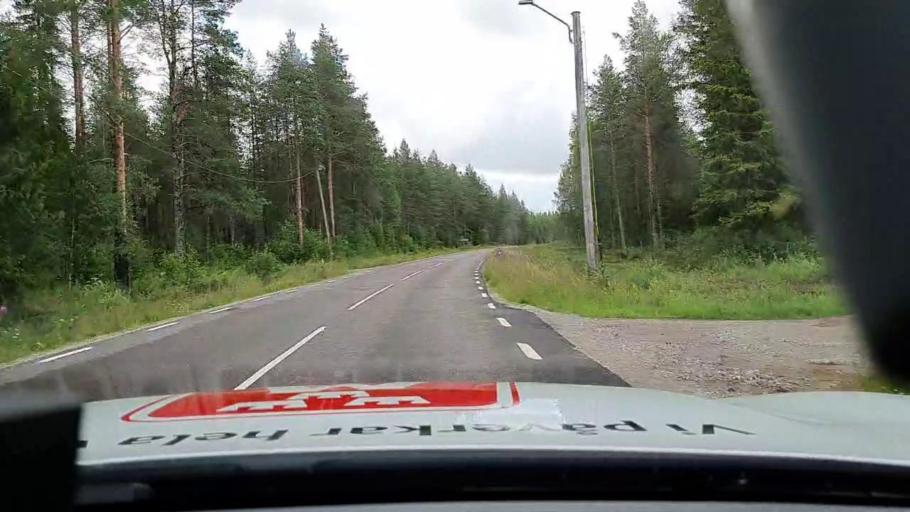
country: SE
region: Norrbotten
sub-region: Overkalix Kommun
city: OEverkalix
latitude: 66.2591
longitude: 22.8513
